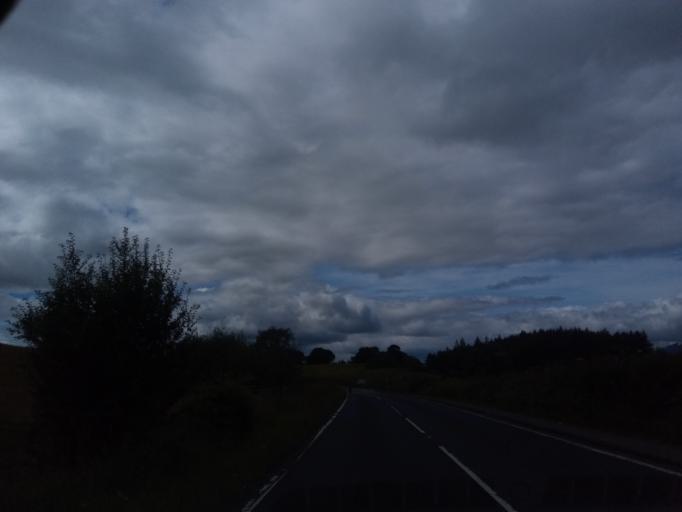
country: GB
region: Scotland
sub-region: Stirling
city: Dunblane
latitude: 56.1901
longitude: -4.0045
